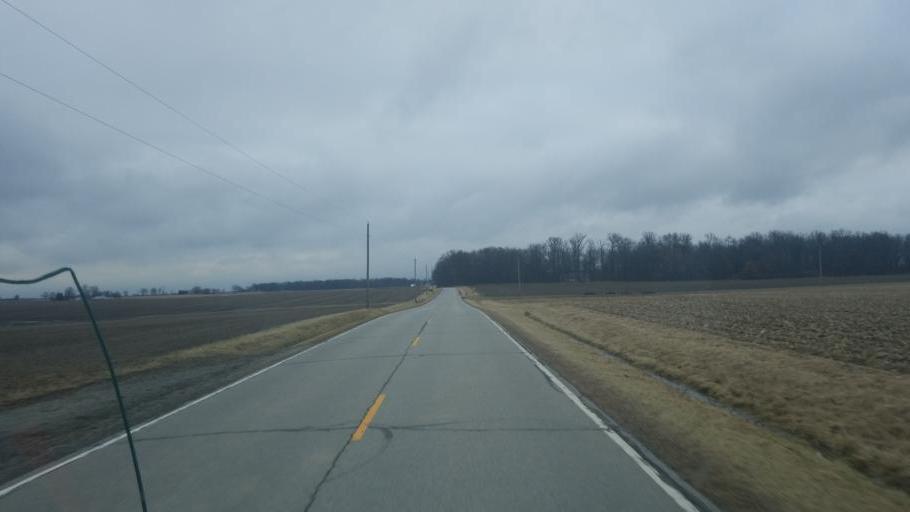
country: US
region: Ohio
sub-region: Crawford County
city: Bucyrus
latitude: 40.7289
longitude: -82.9530
